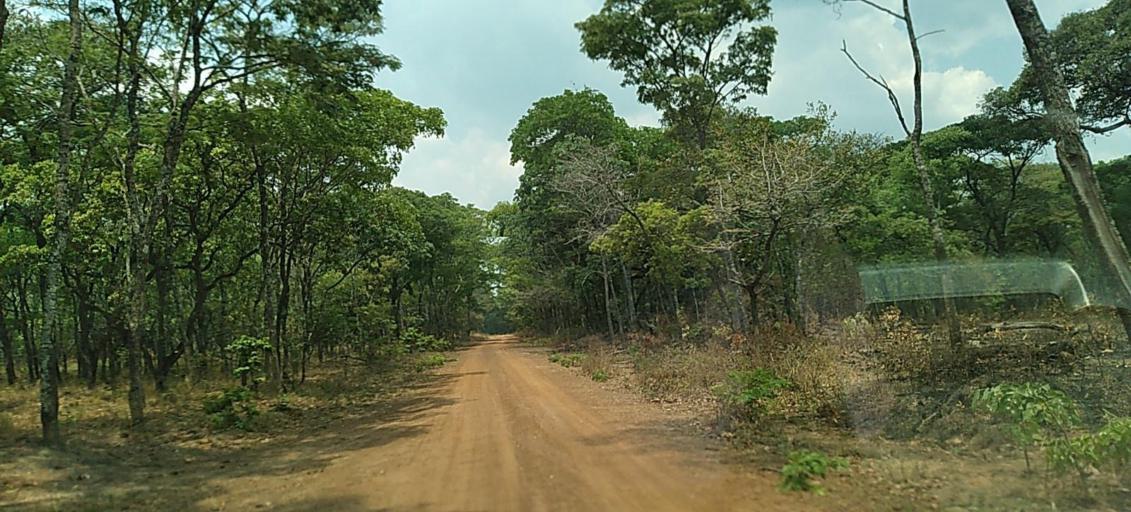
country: ZM
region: Copperbelt
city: Chingola
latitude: -12.7717
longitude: 27.6838
